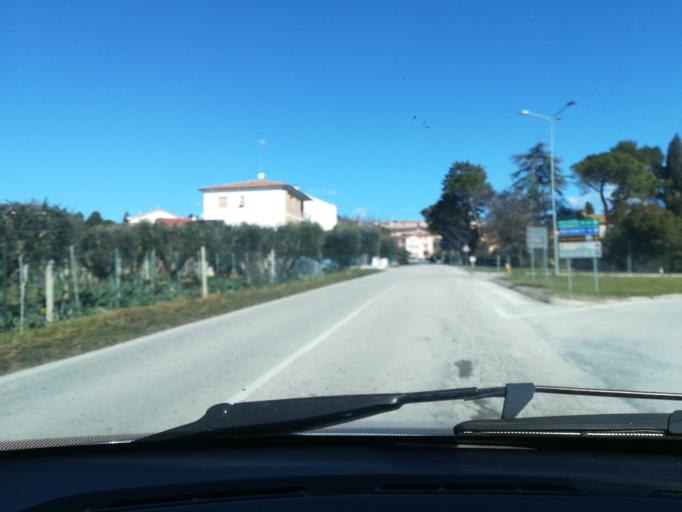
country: IT
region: The Marches
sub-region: Provincia di Macerata
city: Montecassiano
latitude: 43.3603
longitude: 13.4409
